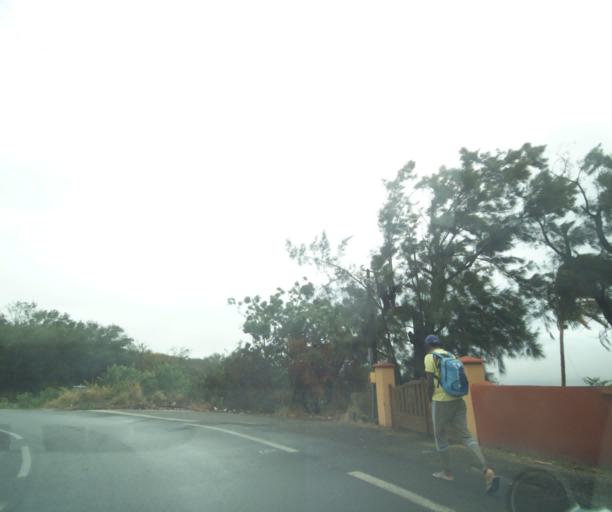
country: RE
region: Reunion
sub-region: Reunion
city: Saint-Paul
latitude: -21.0312
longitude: 55.2841
